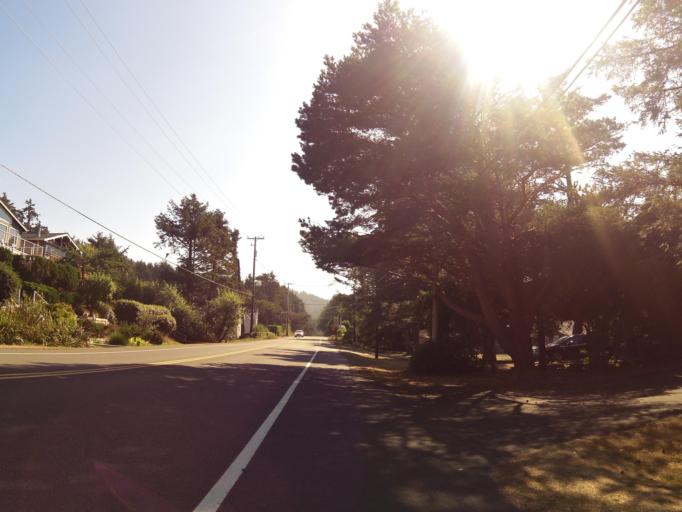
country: US
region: Oregon
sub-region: Clatsop County
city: Cannon Beach
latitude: 45.8690
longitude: -123.9598
